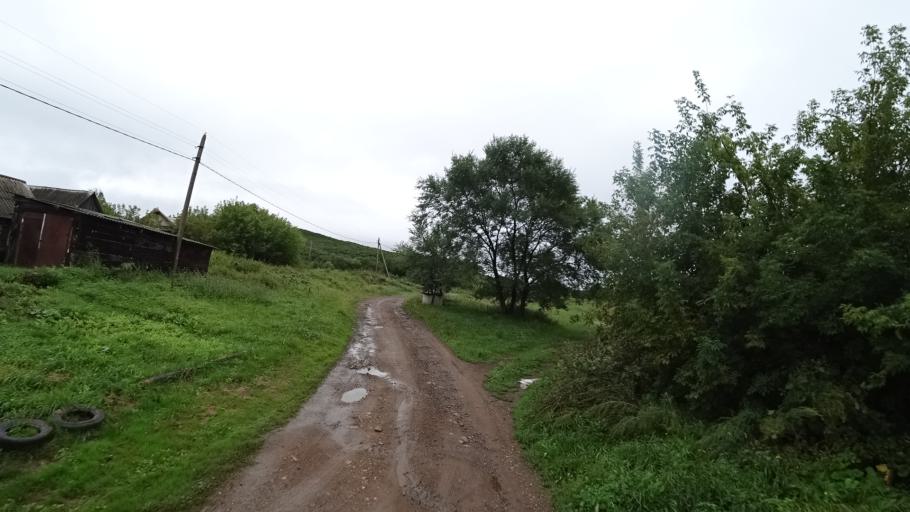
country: RU
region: Primorskiy
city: Monastyrishche
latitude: 44.2727
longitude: 132.4054
